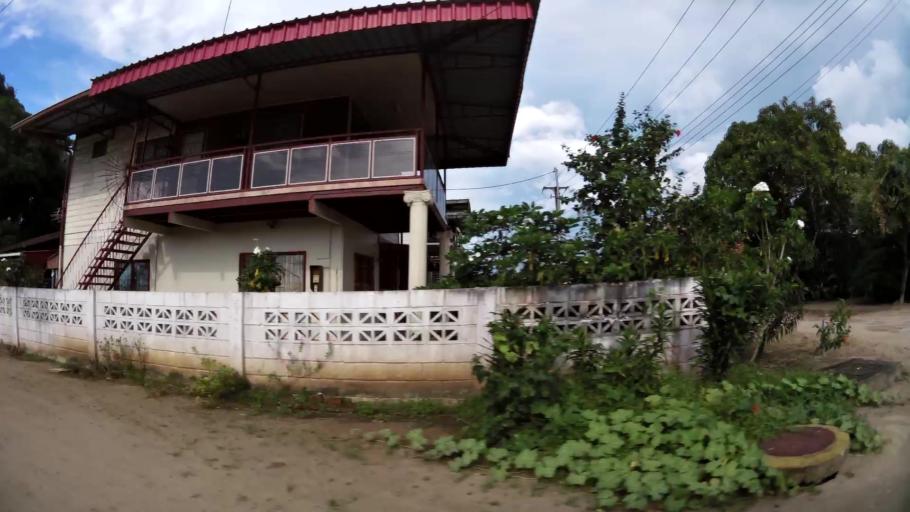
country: SR
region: Paramaribo
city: Paramaribo
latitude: 5.8532
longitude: -55.1834
